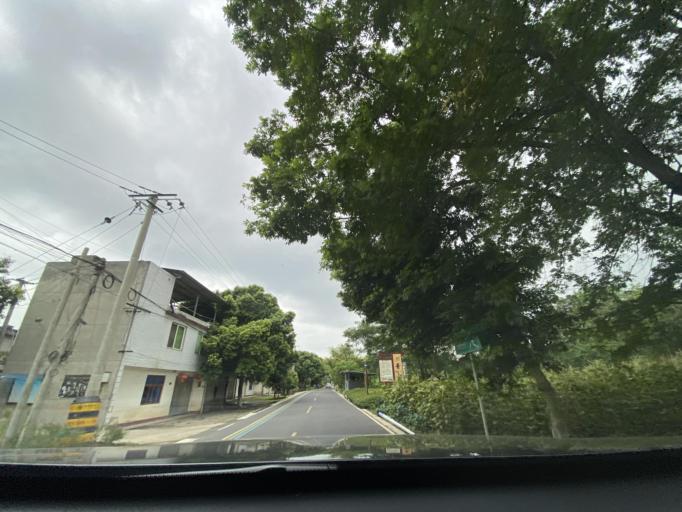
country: CN
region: Sichuan
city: Dongsheng
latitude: 30.4076
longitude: 104.0016
